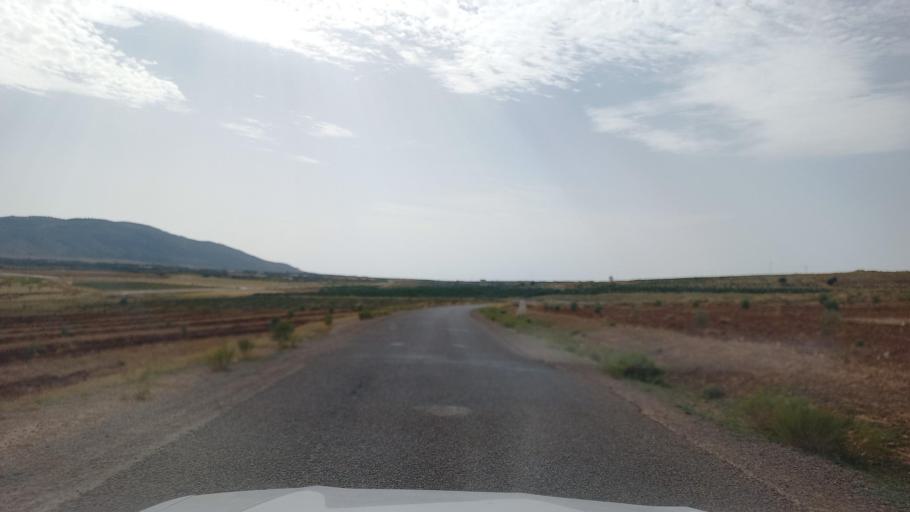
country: TN
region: Al Qasrayn
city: Kasserine
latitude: 35.3602
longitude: 8.8325
